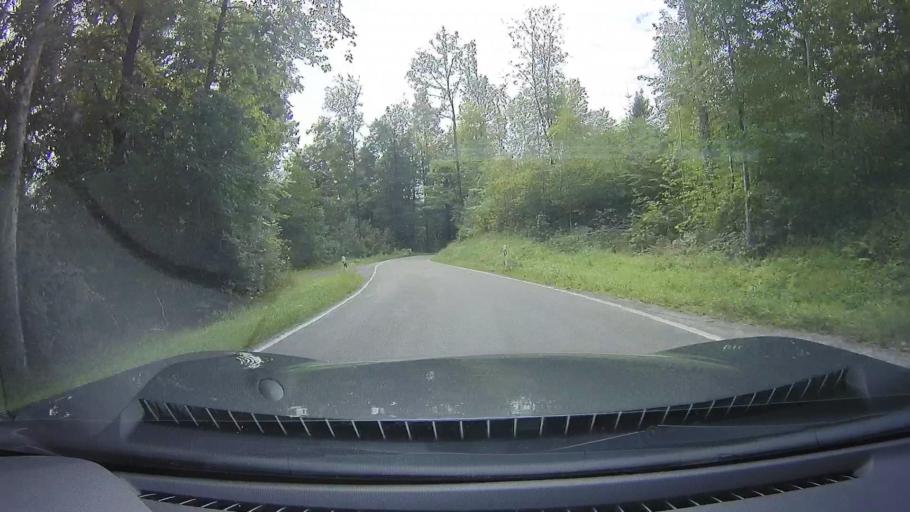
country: DE
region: Baden-Wuerttemberg
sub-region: Regierungsbezirk Stuttgart
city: Spiegelberg
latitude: 49.0405
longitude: 9.4622
